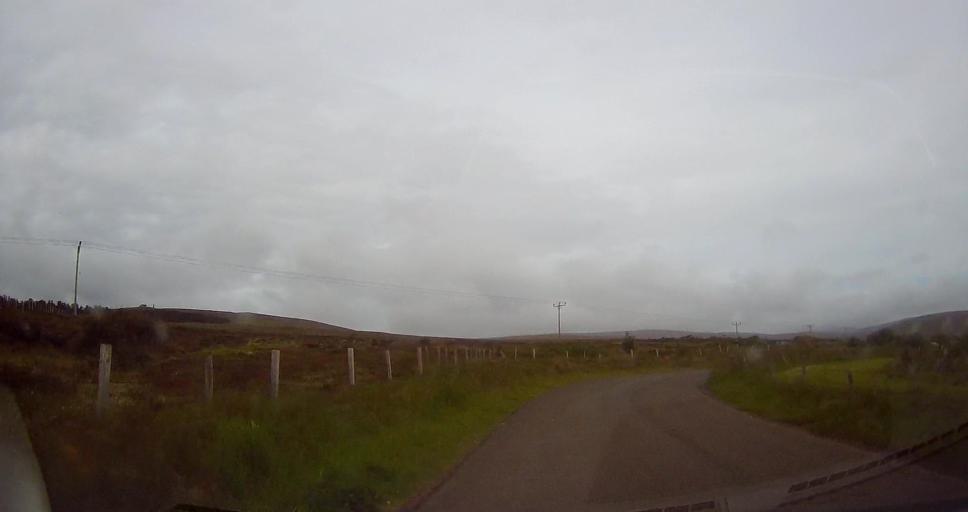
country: GB
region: Scotland
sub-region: Orkney Islands
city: Stromness
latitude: 58.8342
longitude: -3.2120
